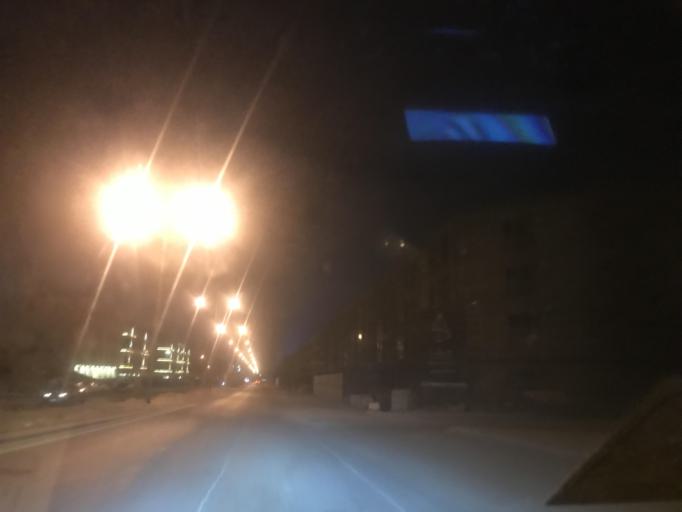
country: SA
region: Ar Riyad
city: Riyadh
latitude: 24.8060
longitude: 46.5907
